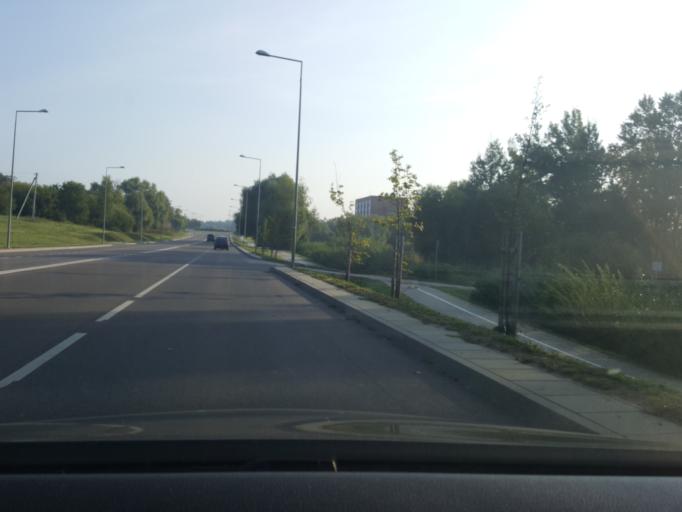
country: LT
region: Alytaus apskritis
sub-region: Alytus
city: Alytus
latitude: 54.4211
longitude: 24.0291
